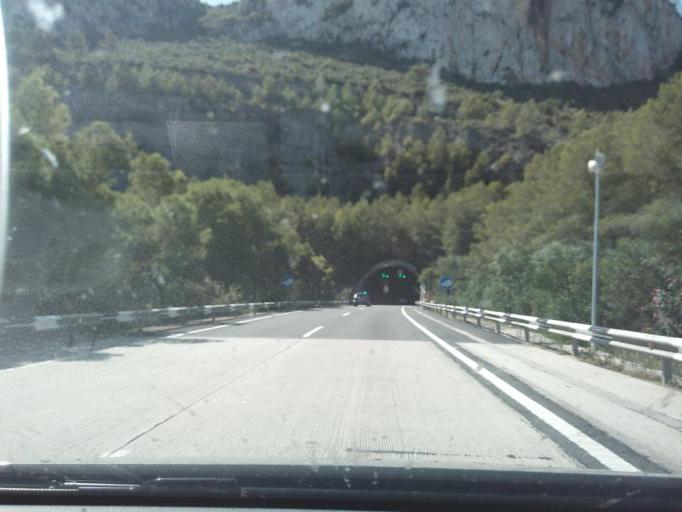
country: ES
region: Valencia
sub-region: Provincia de Valencia
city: Xeresa
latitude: 39.0042
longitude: -0.2250
